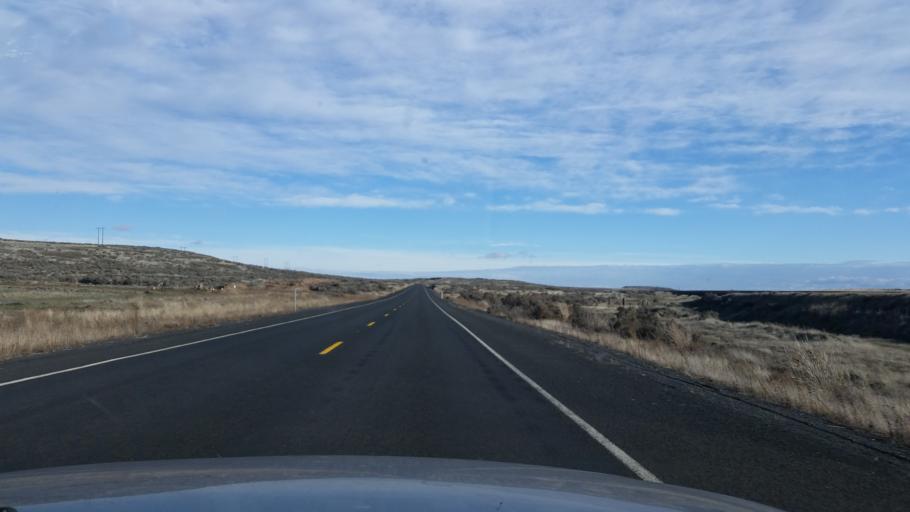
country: US
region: Washington
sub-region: Adams County
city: Ritzville
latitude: 47.3389
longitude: -118.6297
